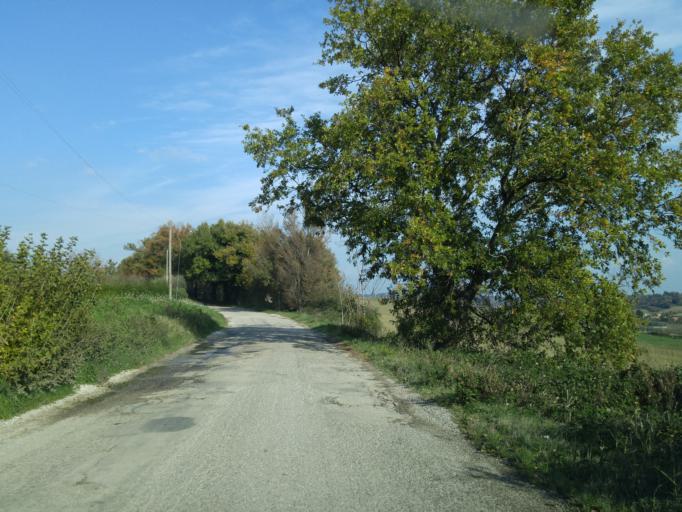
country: IT
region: The Marches
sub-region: Provincia di Pesaro e Urbino
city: Lucrezia
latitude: 43.8125
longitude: 12.9097
